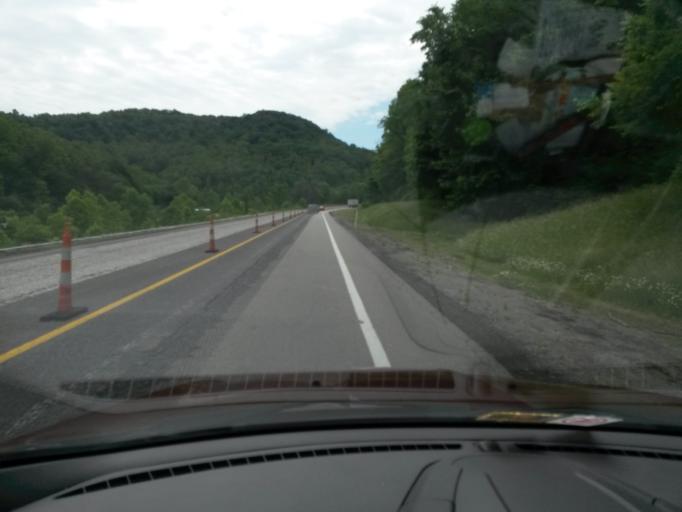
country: US
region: West Virginia
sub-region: Braxton County
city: Sutton
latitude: 38.7477
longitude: -80.6775
